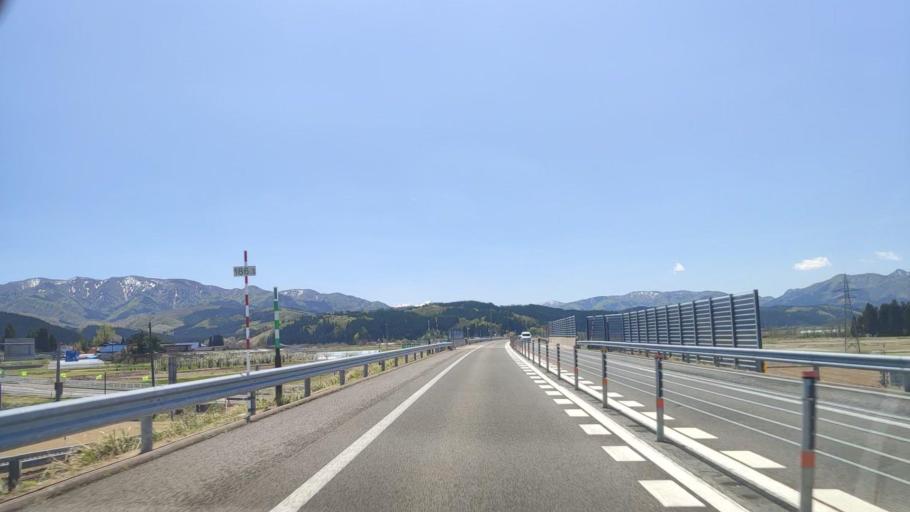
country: JP
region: Akita
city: Yuzawa
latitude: 39.0906
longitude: 140.4841
